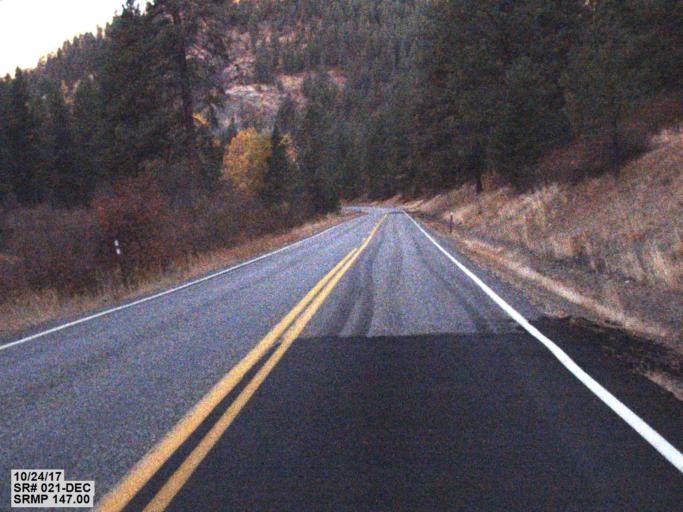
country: US
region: Washington
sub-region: Ferry County
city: Republic
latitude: 48.4731
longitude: -118.7406
